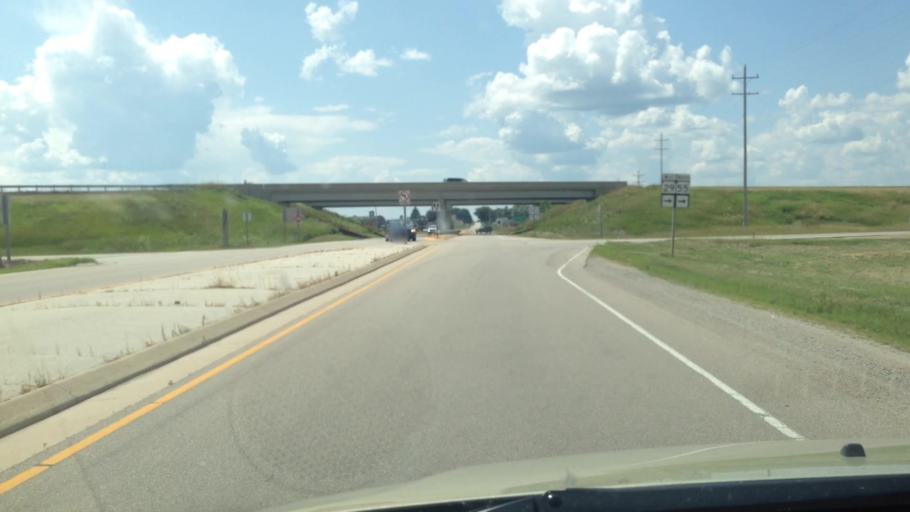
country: US
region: Wisconsin
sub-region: Brown County
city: Pulaski
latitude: 44.6738
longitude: -88.3070
